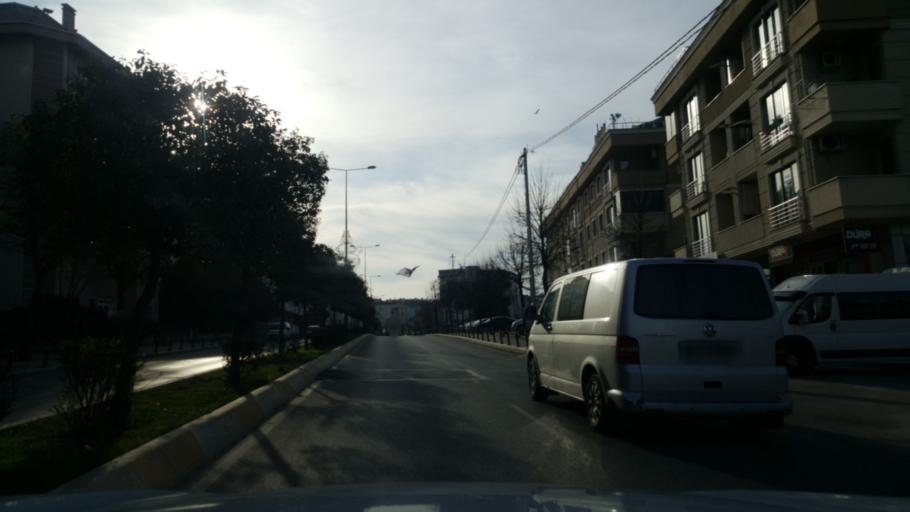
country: TR
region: Istanbul
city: Icmeler
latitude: 40.8261
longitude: 29.3128
